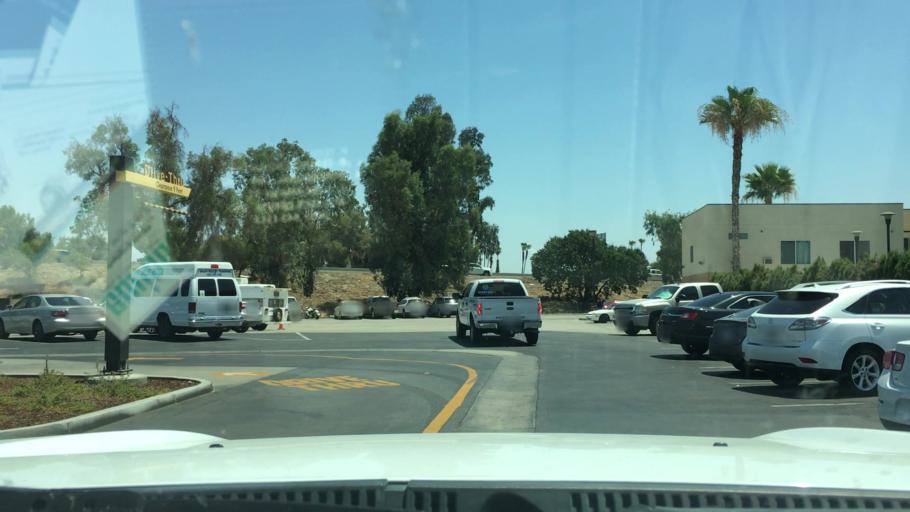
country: US
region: California
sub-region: Kern County
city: Bakersfield
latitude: 35.3669
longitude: -119.0429
